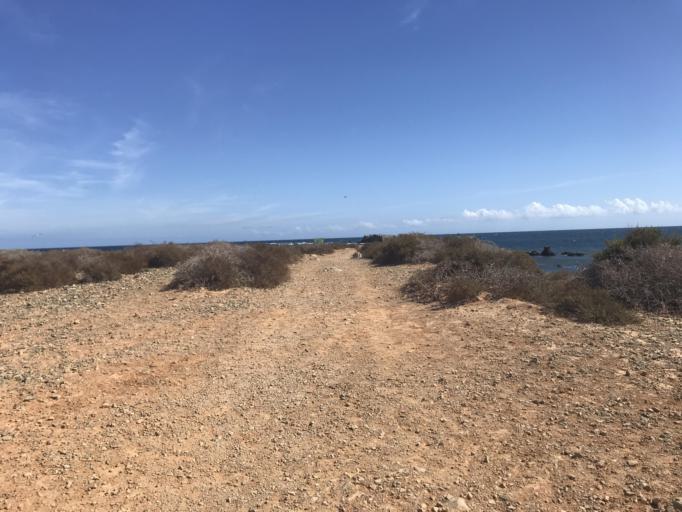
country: ES
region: Valencia
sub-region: Provincia de Alicante
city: Santa Pola
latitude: 38.1635
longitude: -0.4661
